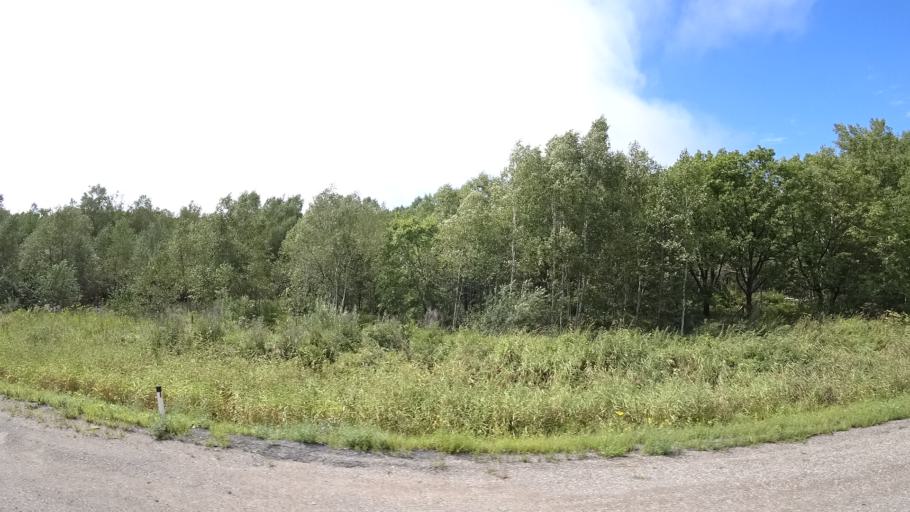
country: RU
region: Primorskiy
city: Lyalichi
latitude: 44.1182
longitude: 132.4193
